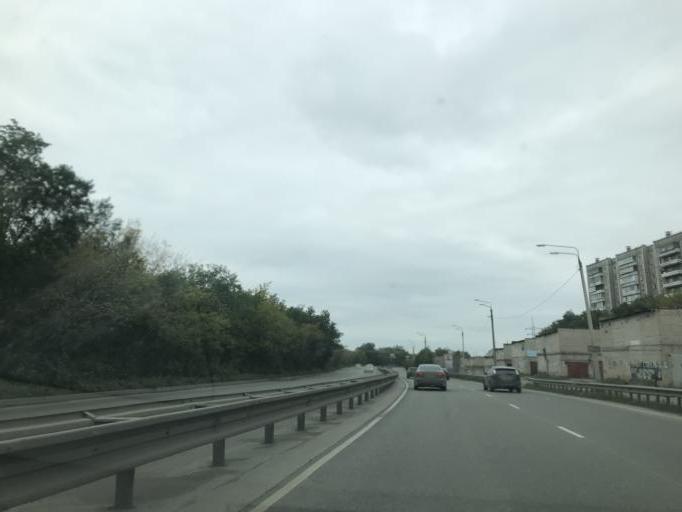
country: RU
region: Chelyabinsk
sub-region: Gorod Chelyabinsk
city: Chelyabinsk
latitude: 55.1728
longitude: 61.4261
